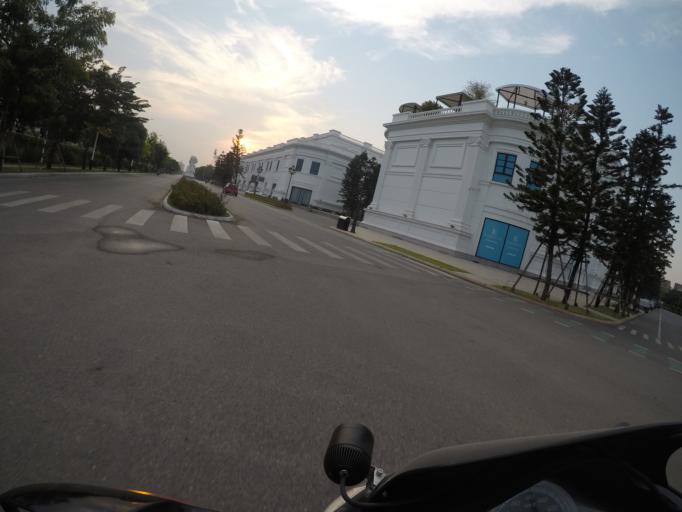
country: VN
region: Ha Noi
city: Trau Quy
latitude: 21.0457
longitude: 105.9187
